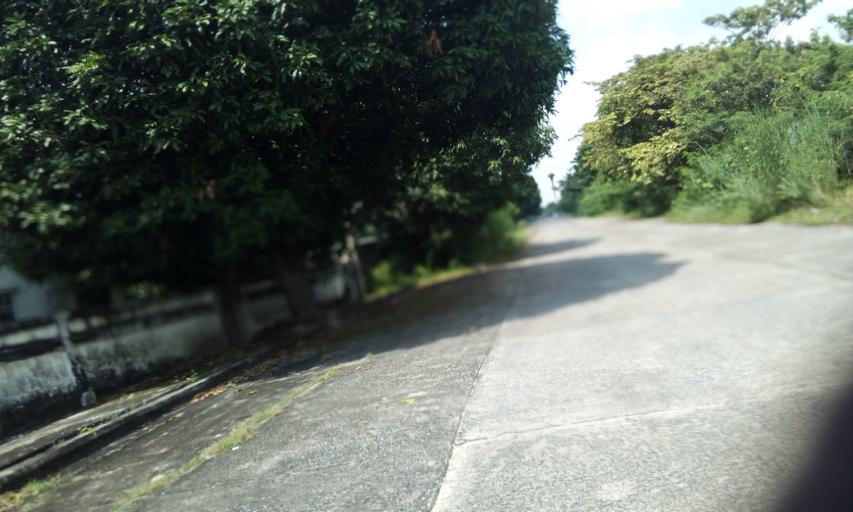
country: TH
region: Pathum Thani
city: Ban Rangsit
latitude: 14.0475
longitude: 100.8312
